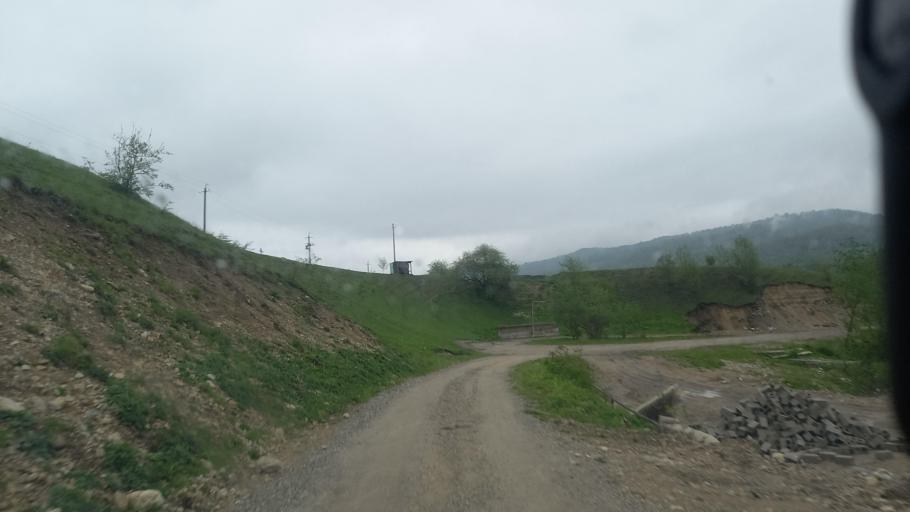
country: RU
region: Kabardino-Balkariya
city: Babugent
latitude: 43.2493
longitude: 43.5295
